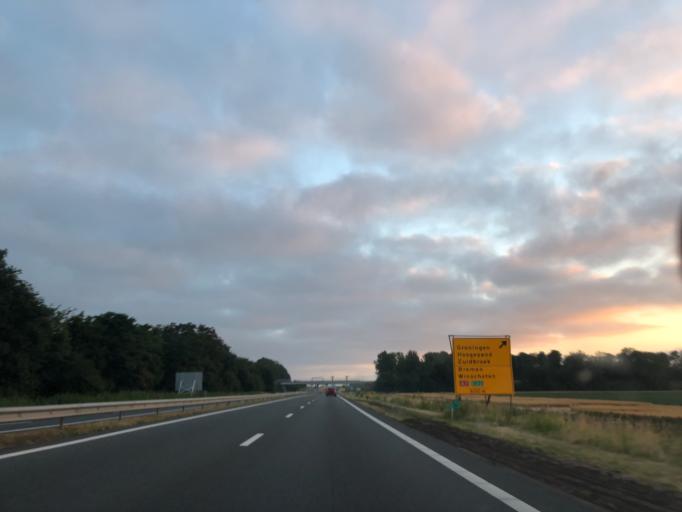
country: NL
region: Groningen
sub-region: Gemeente Veendam
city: Veendam
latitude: 53.1578
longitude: 6.8960
